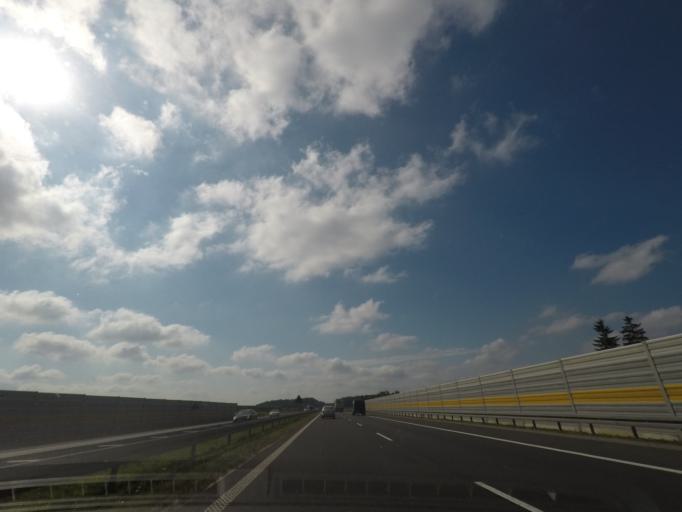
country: PL
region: Pomeranian Voivodeship
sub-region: Powiat starogardzki
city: Smetowo Graniczne
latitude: 53.6822
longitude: 18.6334
